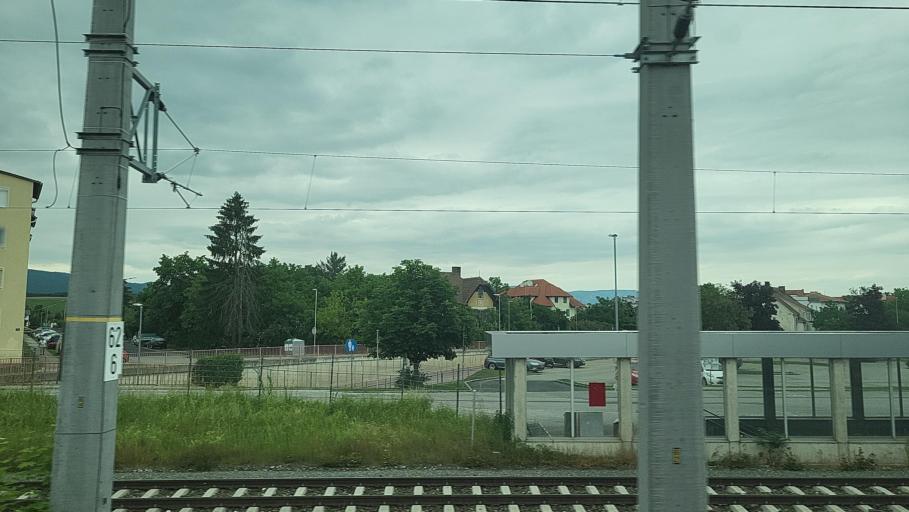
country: AT
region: Lower Austria
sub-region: Politischer Bezirk Neunkirchen
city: Neunkirchen
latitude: 47.7314
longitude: 16.0843
